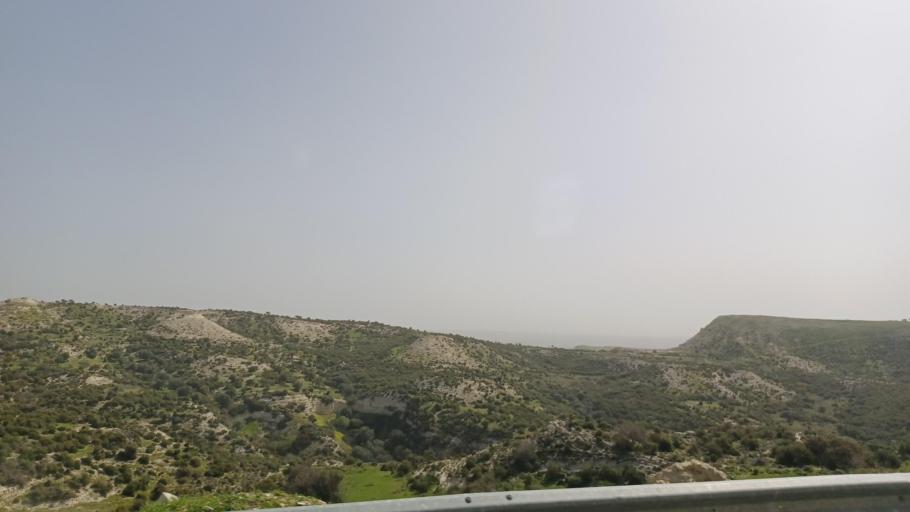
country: CY
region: Limassol
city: Pissouri
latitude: 34.6947
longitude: 32.7063
